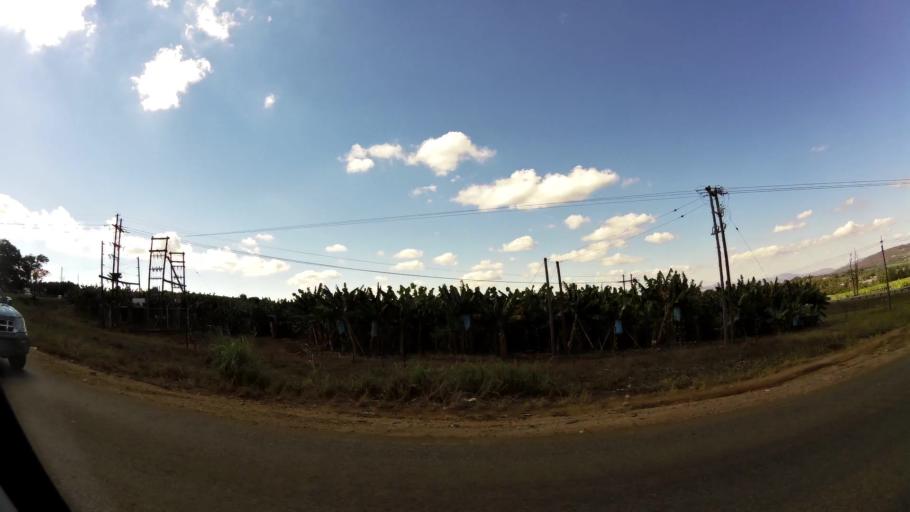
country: ZA
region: Limpopo
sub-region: Mopani District Municipality
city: Tzaneen
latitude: -23.8132
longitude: 30.1729
